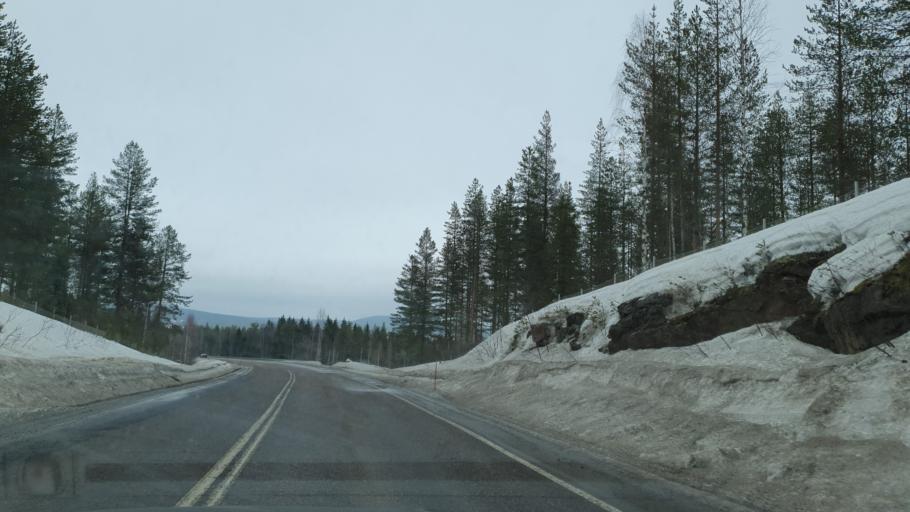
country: FI
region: Lapland
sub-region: Torniolaakso
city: Pello
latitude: 66.8905
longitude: 24.0858
